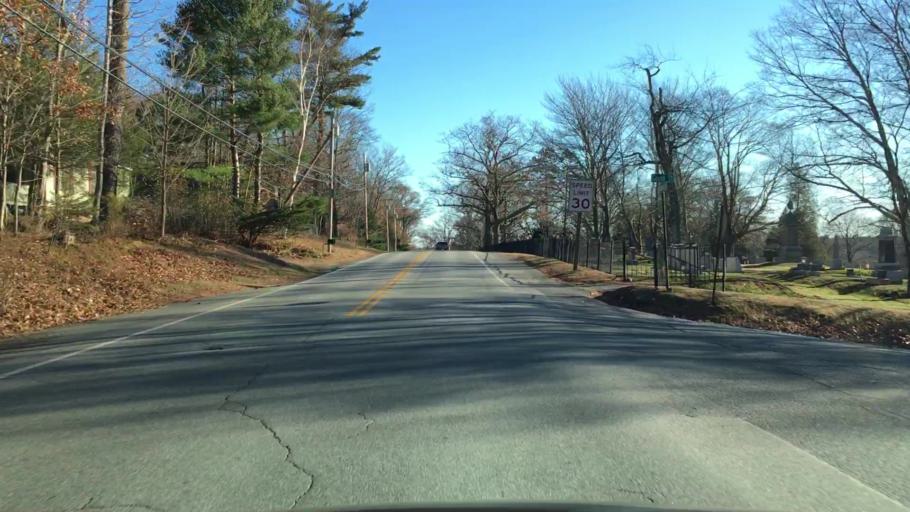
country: US
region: Maine
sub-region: Knox County
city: Camden
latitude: 44.2196
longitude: -69.0741
